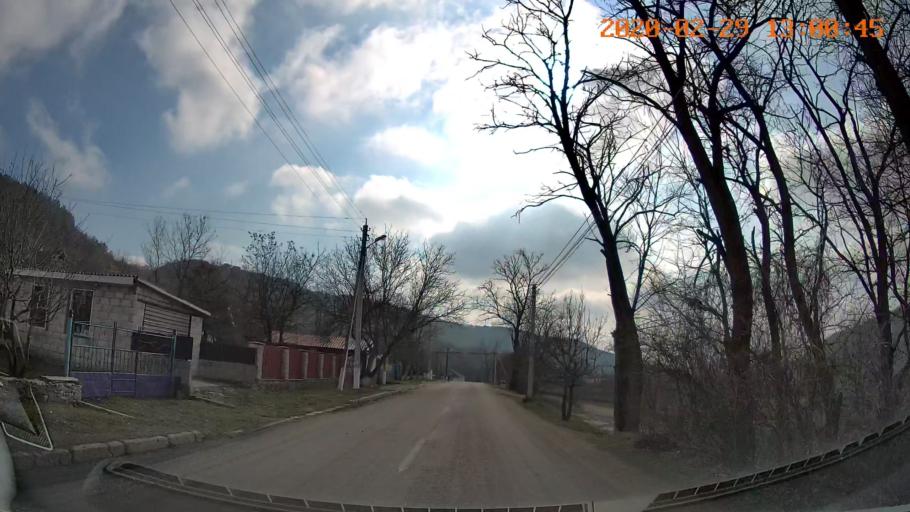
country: MD
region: Telenesti
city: Camenca
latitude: 48.0499
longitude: 28.7213
